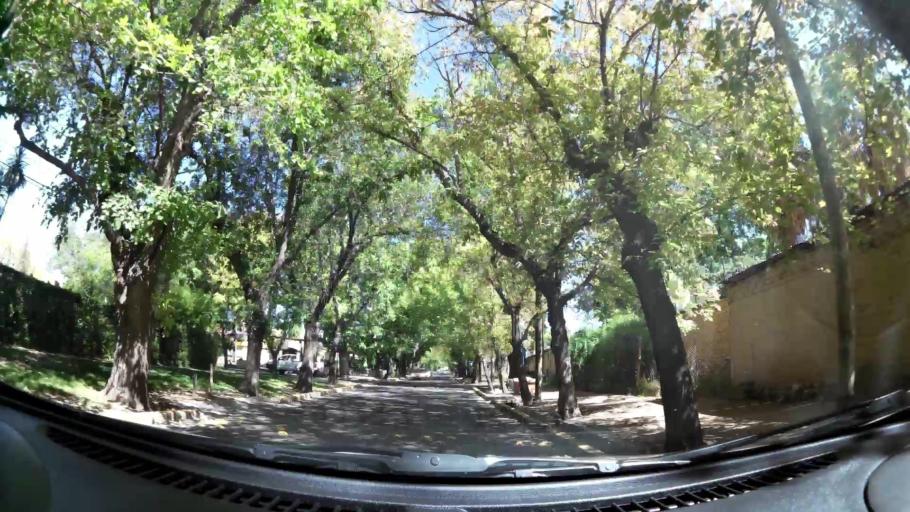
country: AR
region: Mendoza
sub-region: Departamento de Godoy Cruz
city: Godoy Cruz
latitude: -32.9615
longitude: -68.8605
